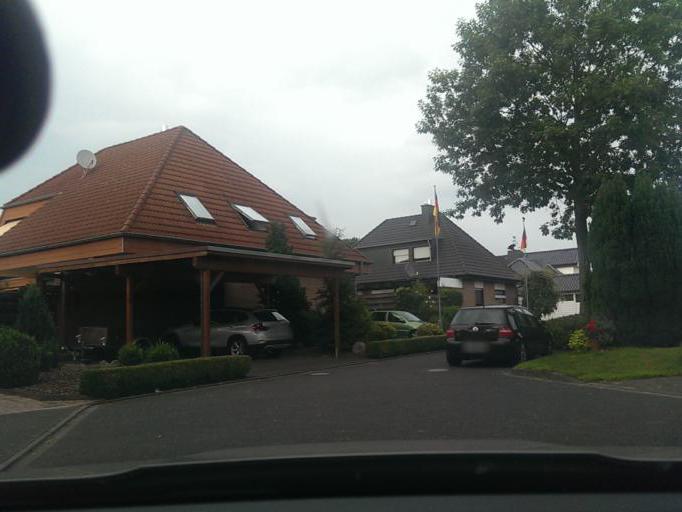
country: DE
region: North Rhine-Westphalia
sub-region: Regierungsbezirk Detmold
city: Delbruck
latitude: 51.7689
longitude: 8.5453
